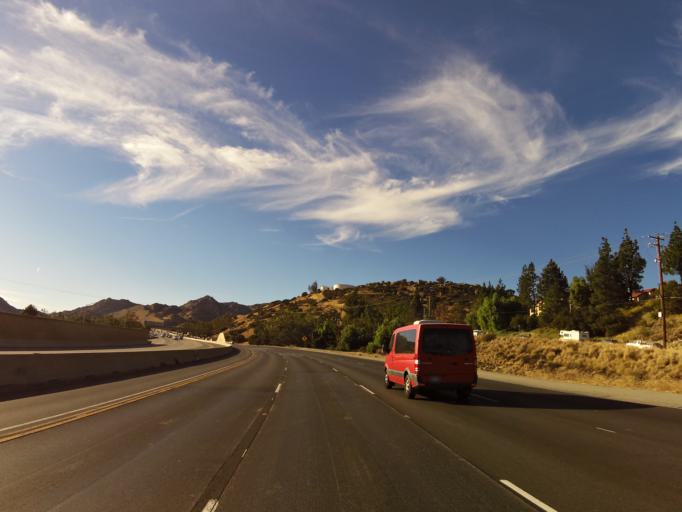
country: US
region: California
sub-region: Los Angeles County
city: Chatsworth
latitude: 34.2779
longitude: -118.6049
